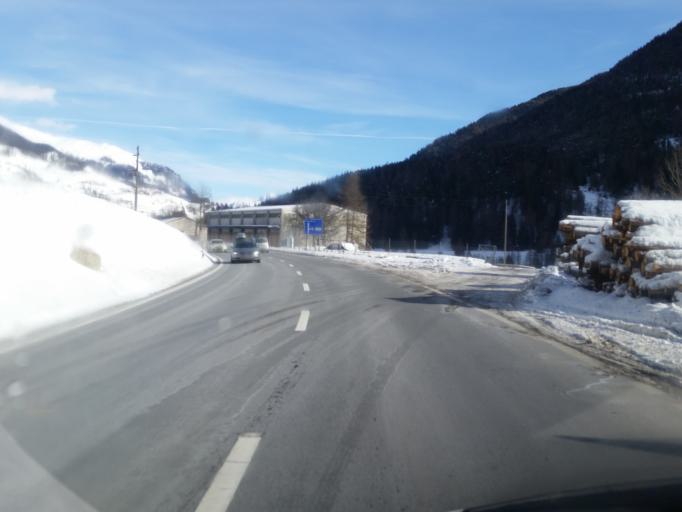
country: CH
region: Grisons
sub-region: Inn District
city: Zernez
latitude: 46.7638
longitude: 10.1040
